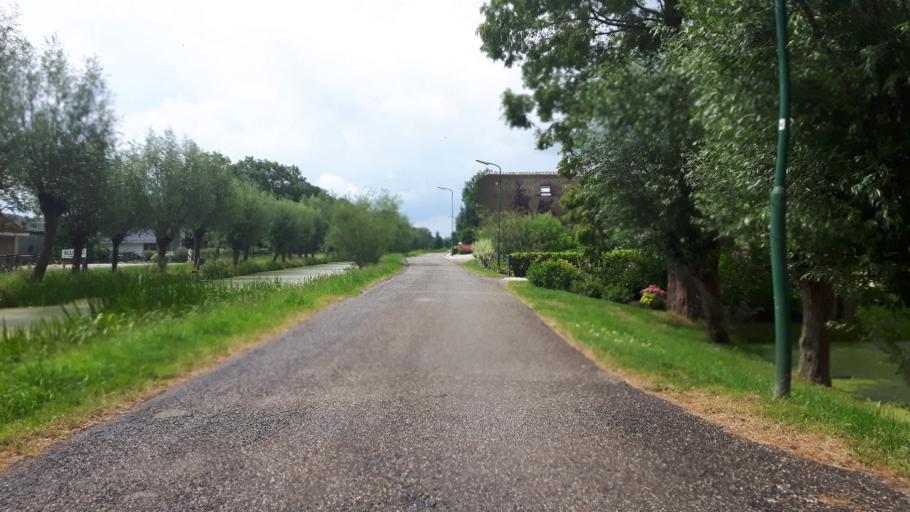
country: NL
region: Utrecht
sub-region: Gemeente Oudewater
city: Oudewater
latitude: 51.9844
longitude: 4.8716
